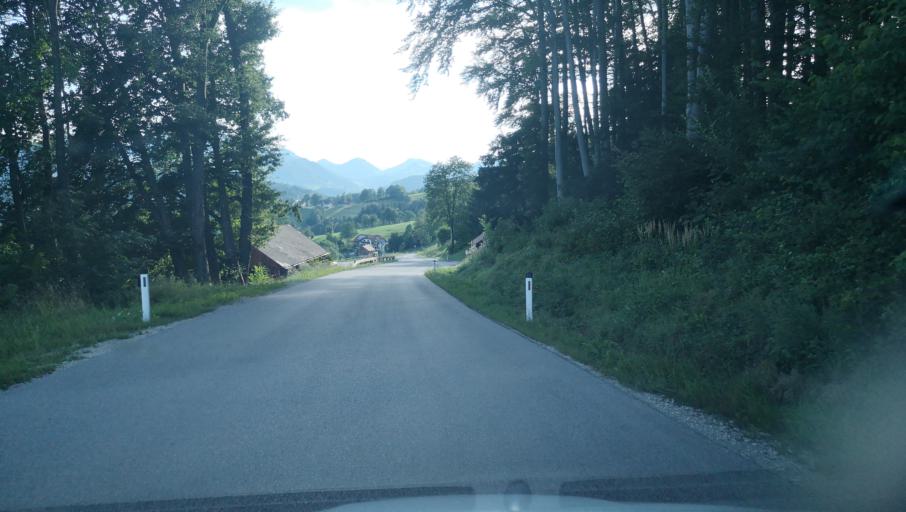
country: AT
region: Lower Austria
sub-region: Waidhofen an der Ybbs Stadt
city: Waidhofen an der Ybbs
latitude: 47.9752
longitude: 14.8219
